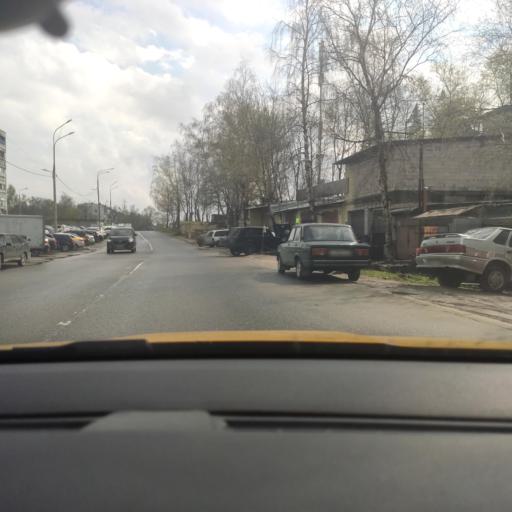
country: RU
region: Moskovskaya
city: Cherkizovo
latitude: 55.9423
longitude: 37.7731
